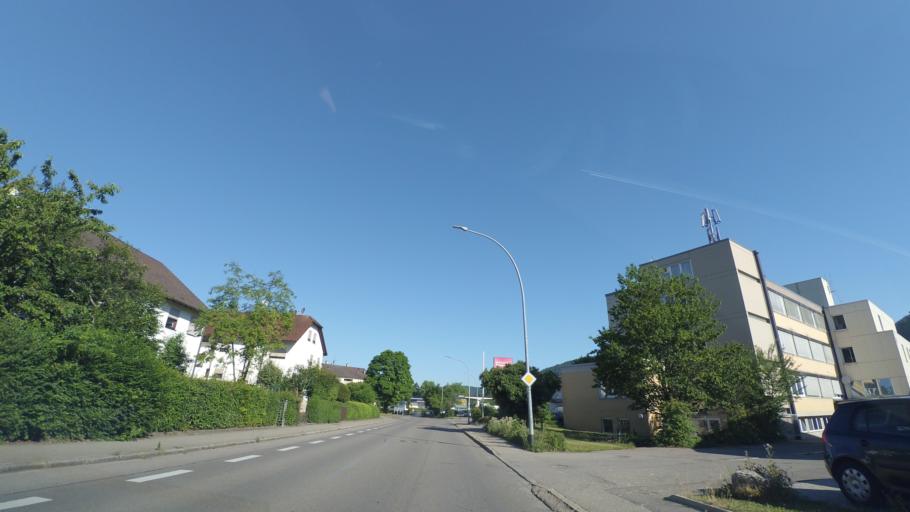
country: DE
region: Baden-Wuerttemberg
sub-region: Regierungsbezirk Stuttgart
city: Murrhardt
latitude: 48.9838
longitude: 9.5583
